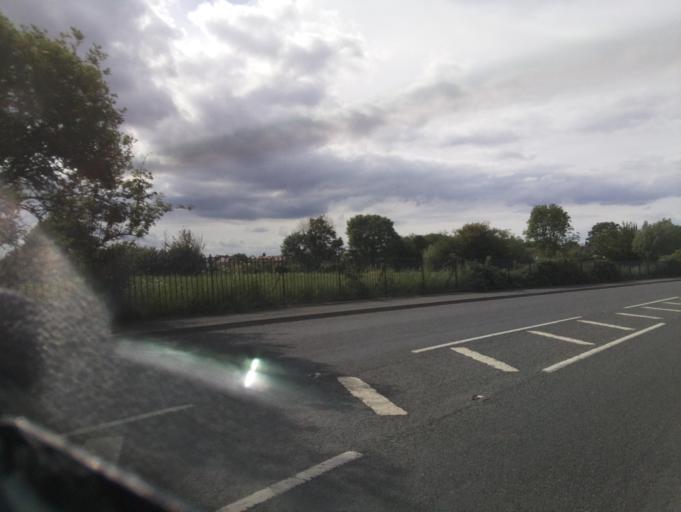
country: GB
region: England
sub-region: Worcestershire
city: Pershore
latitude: 52.1050
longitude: -2.0719
